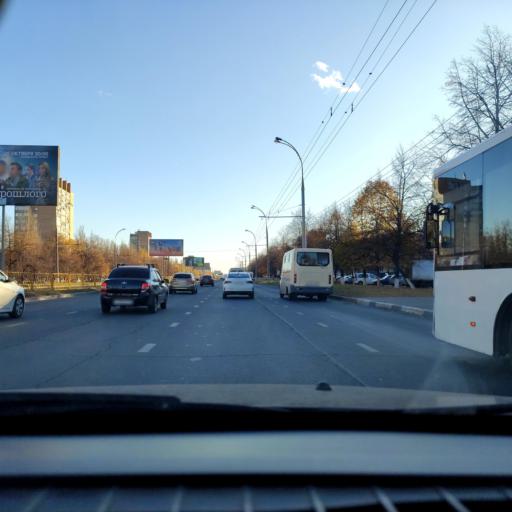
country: RU
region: Samara
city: Tol'yatti
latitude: 53.5254
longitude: 49.2963
